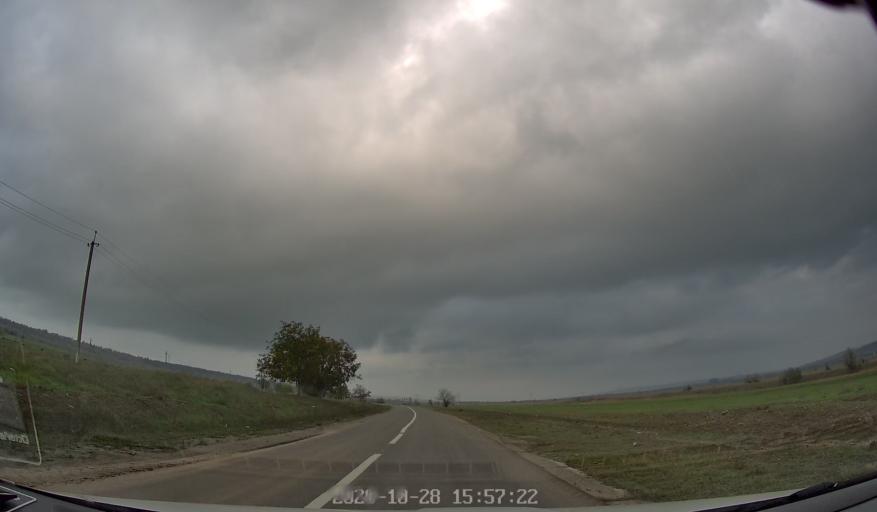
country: UA
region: Odessa
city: Zaliznychne
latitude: 45.7532
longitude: 28.5739
